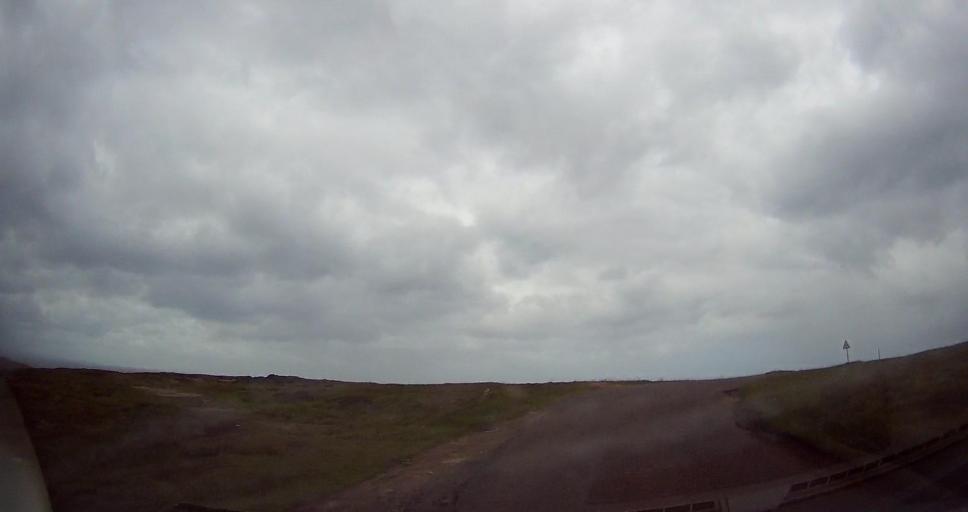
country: GB
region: Scotland
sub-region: Highland
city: Thurso
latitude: 58.6683
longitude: -3.3768
